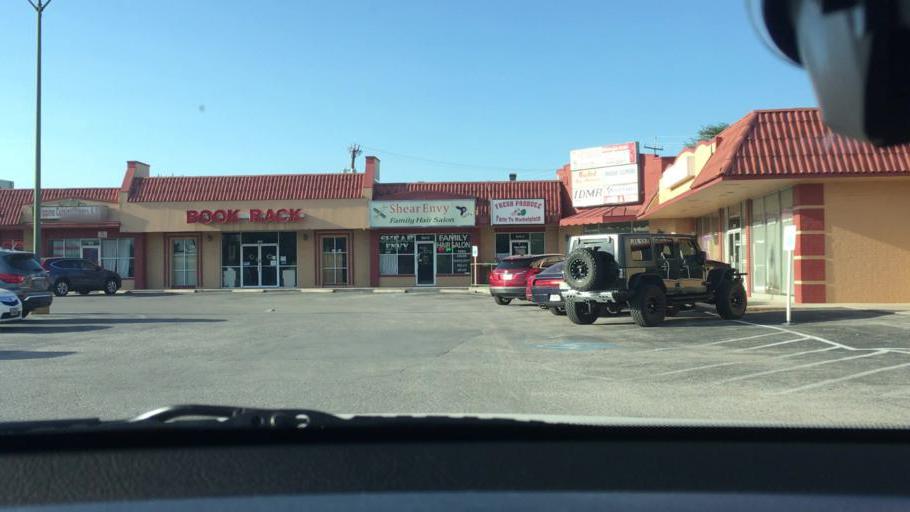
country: US
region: Texas
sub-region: Bexar County
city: Universal City
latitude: 29.5496
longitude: -98.2936
